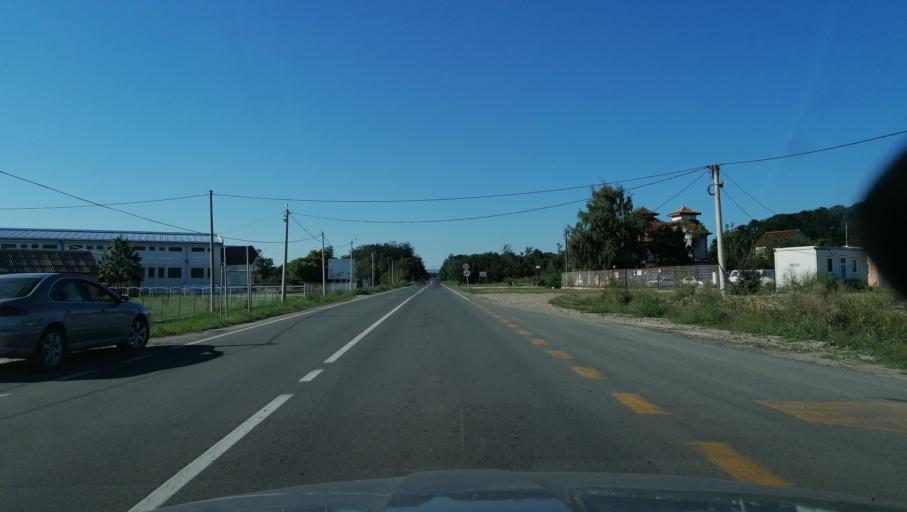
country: RS
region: Central Serbia
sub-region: Raski Okrug
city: Kraljevo
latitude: 43.8083
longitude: 20.6149
